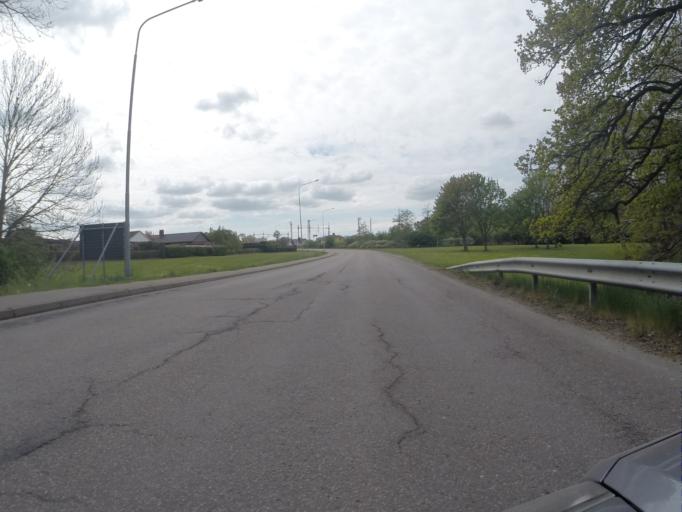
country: SE
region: Skane
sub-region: Bjuvs Kommun
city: Billesholm
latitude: 56.0600
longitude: 12.9780
